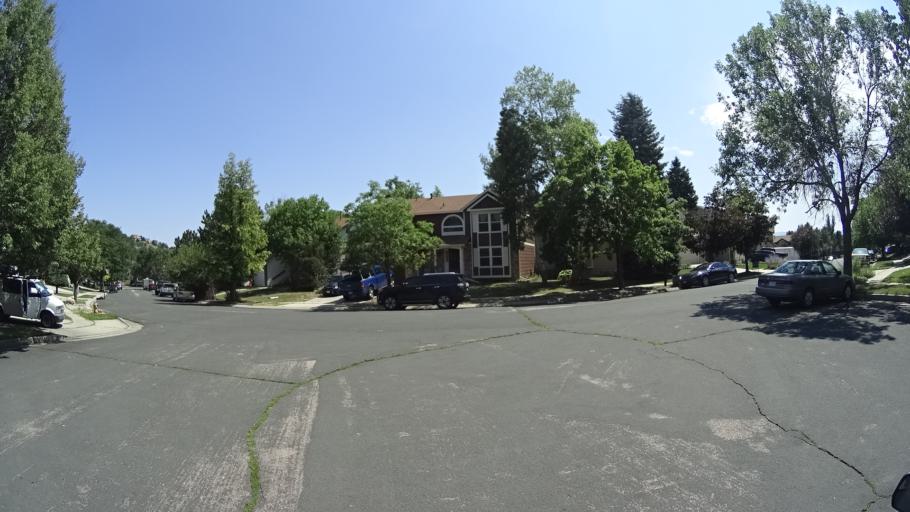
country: US
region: Colorado
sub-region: El Paso County
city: Air Force Academy
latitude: 38.9319
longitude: -104.8683
